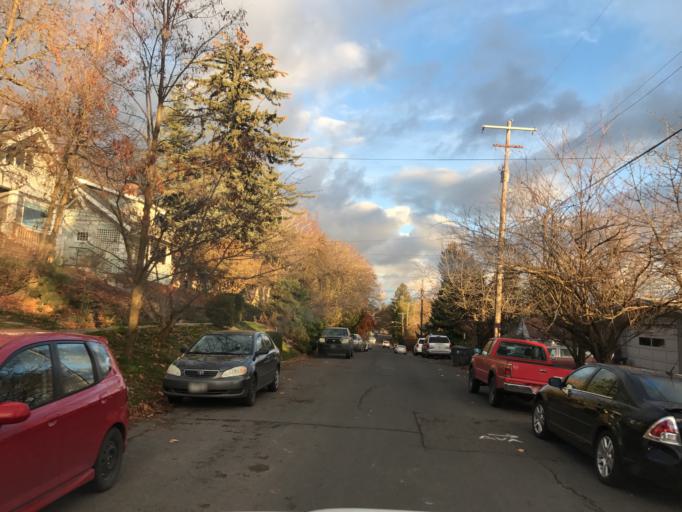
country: US
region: Idaho
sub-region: Latah County
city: Moscow
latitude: 46.7360
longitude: -117.0118
